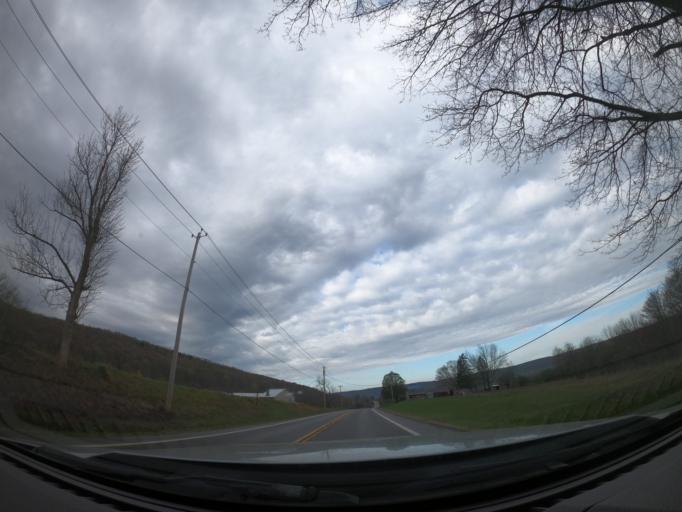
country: US
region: New York
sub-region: Madison County
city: Cazenovia
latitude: 42.7494
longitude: -75.9238
